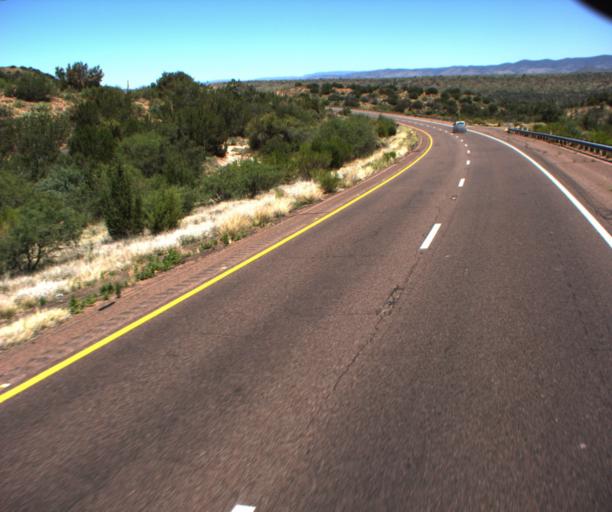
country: US
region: Arizona
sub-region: Gila County
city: Tonto Basin
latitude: 34.0168
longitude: -111.3583
